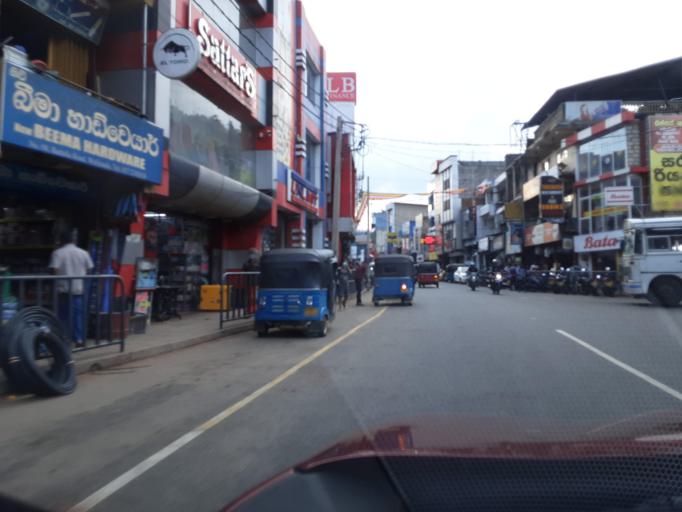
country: LK
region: Uva
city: Haputale
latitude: 6.9047
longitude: 80.9120
